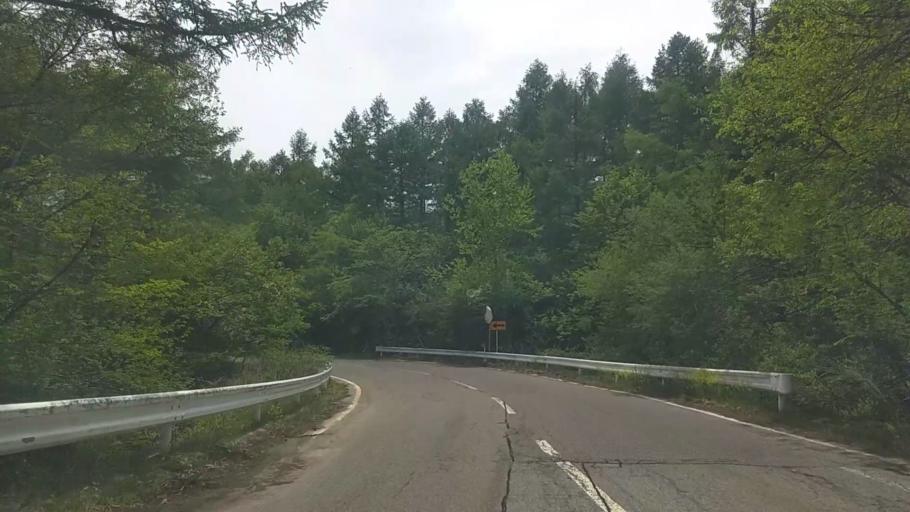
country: JP
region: Nagano
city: Saku
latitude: 36.1069
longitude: 138.3980
